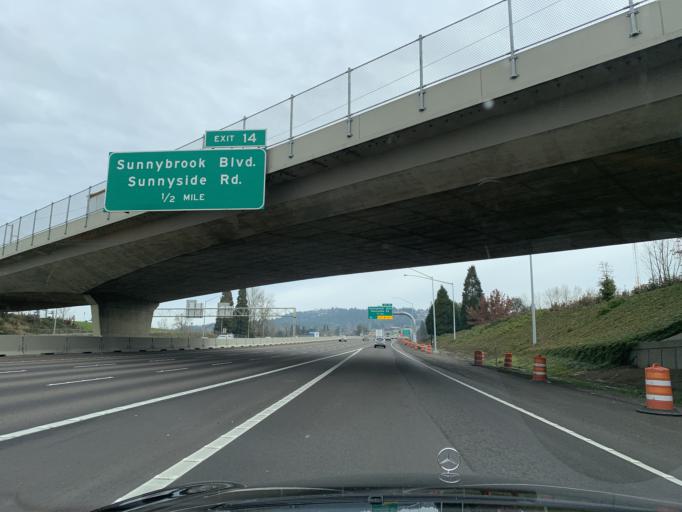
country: US
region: Oregon
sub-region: Clackamas County
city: Clackamas
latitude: 45.4198
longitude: -122.5728
